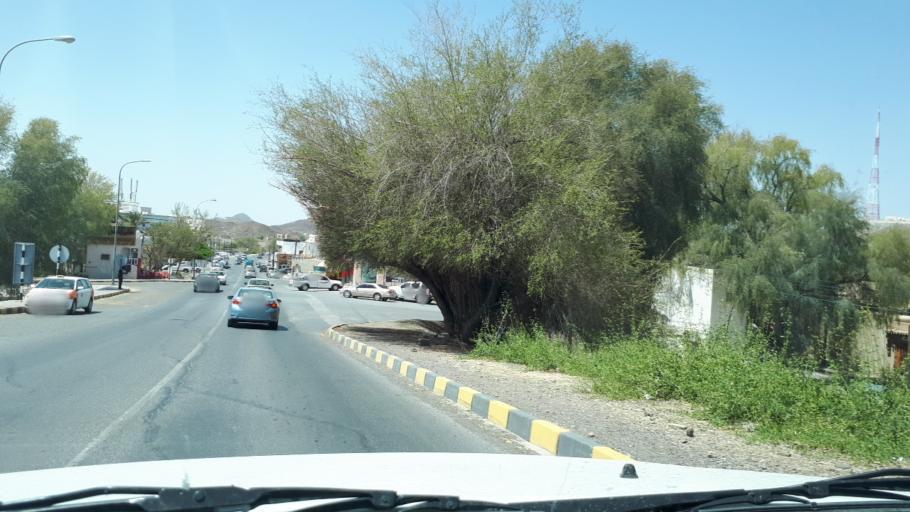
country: OM
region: Muhafazat ad Dakhiliyah
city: Bahla'
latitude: 22.9645
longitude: 57.2998
